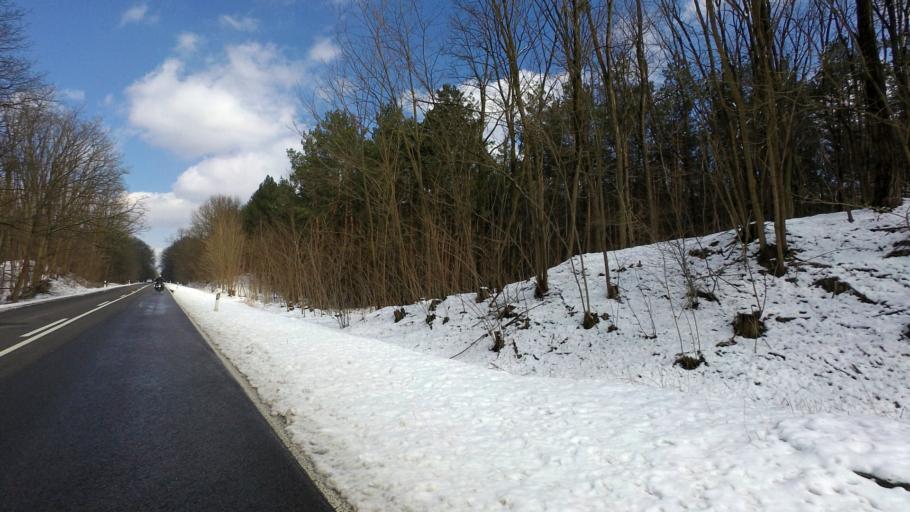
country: DE
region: Brandenburg
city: Eberswalde
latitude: 52.7980
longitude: 13.8366
